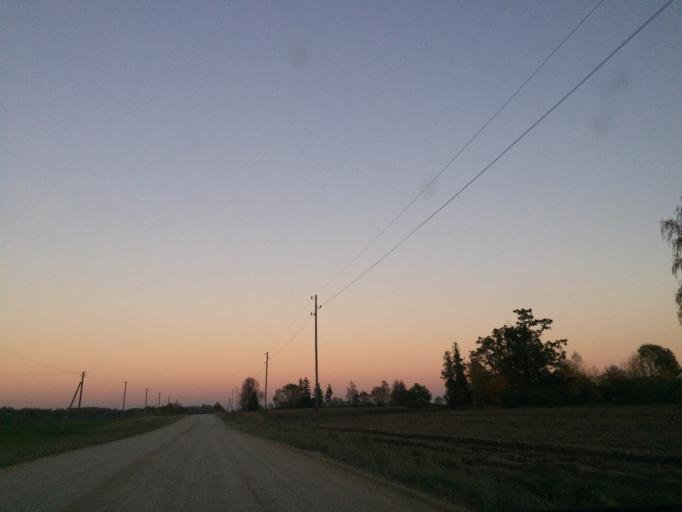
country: LT
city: Akmene
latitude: 56.3771
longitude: 22.6672
